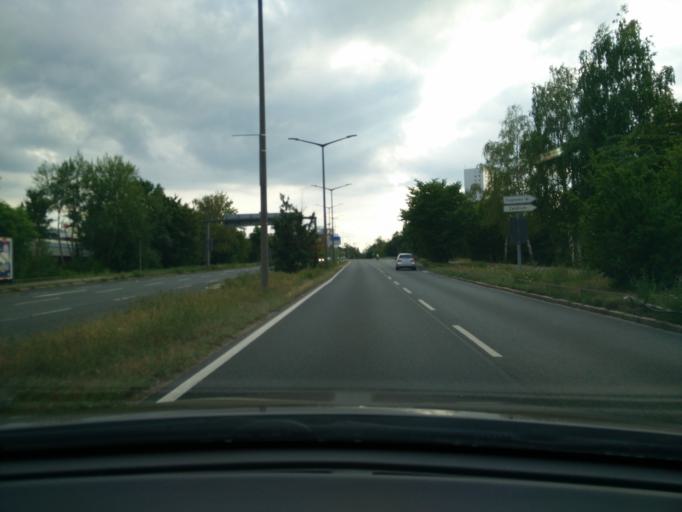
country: DE
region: Bavaria
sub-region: Regierungsbezirk Mittelfranken
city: Nuernberg
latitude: 49.4161
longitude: 11.1212
